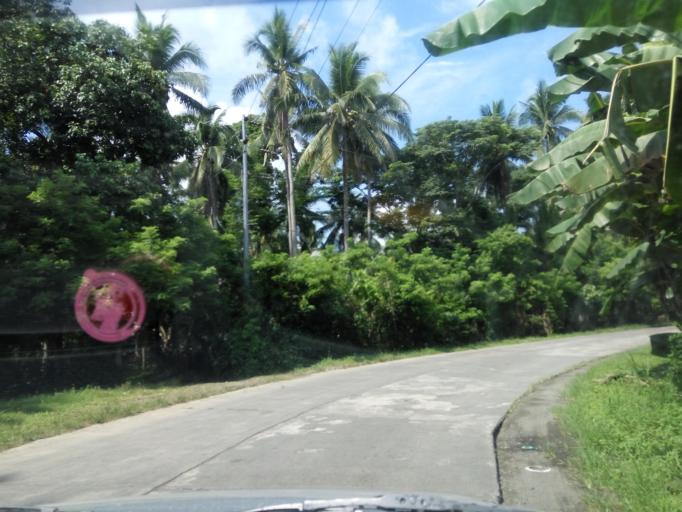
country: PH
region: Central Luzon
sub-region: Province of Aurora
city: Maria Aurora
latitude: 15.8321
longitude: 121.5301
